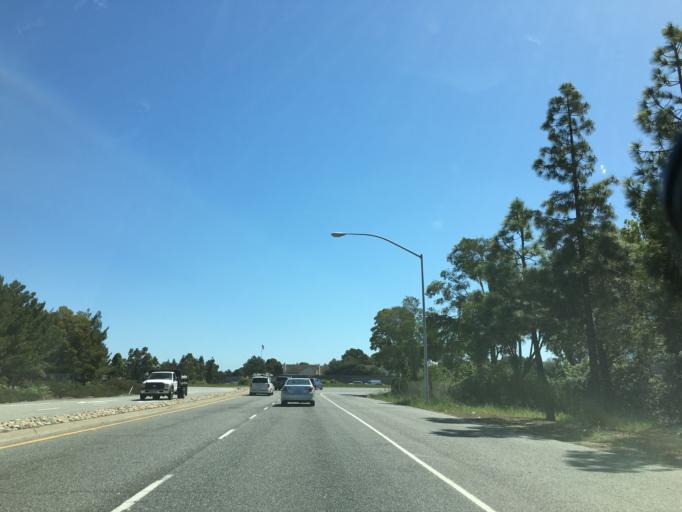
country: US
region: California
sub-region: San Mateo County
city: Foster City
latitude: 37.5585
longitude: -122.2851
